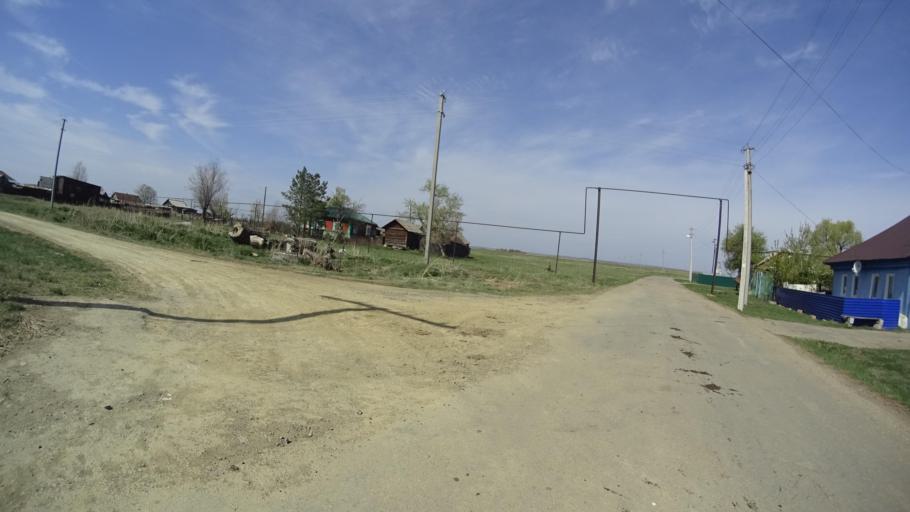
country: RU
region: Chelyabinsk
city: Chesma
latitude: 53.7995
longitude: 61.0179
